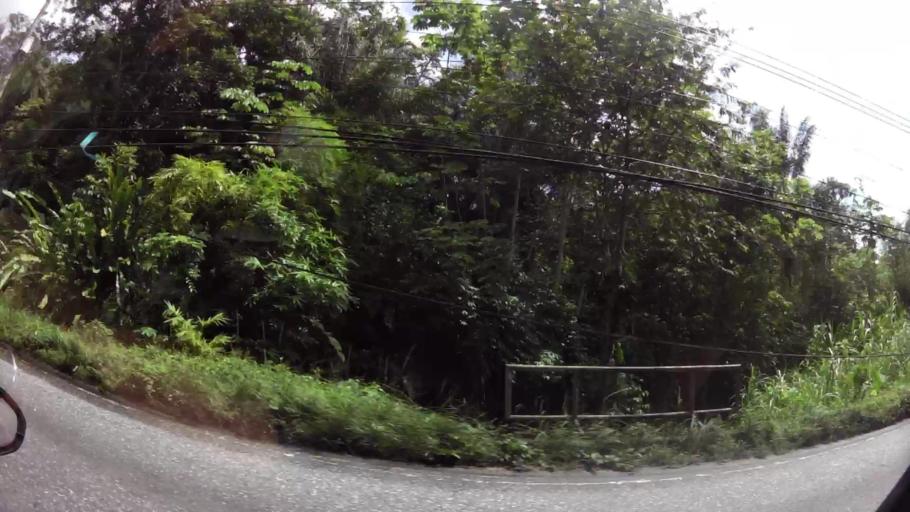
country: TT
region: Borough of Arima
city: Arima
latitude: 10.6318
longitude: -61.2981
